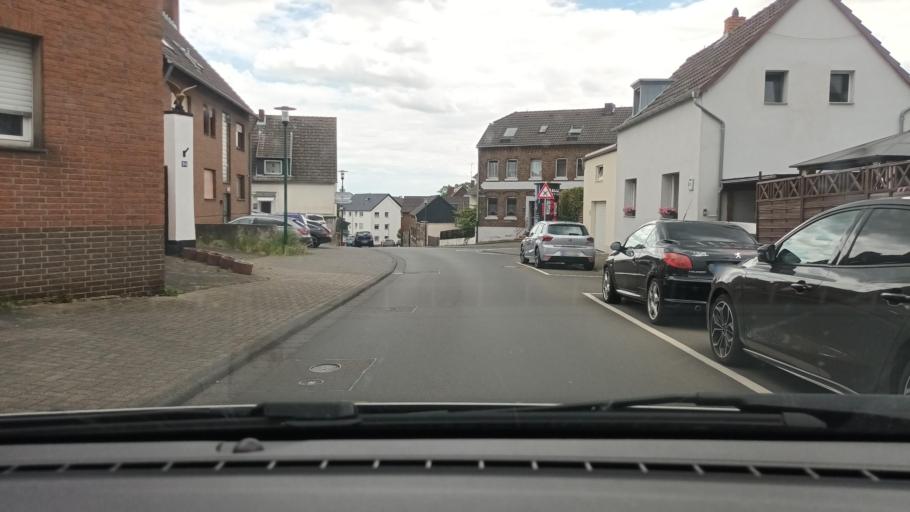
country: DE
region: North Rhine-Westphalia
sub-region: Regierungsbezirk Koln
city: Hurth
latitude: 50.8632
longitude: 6.8804
